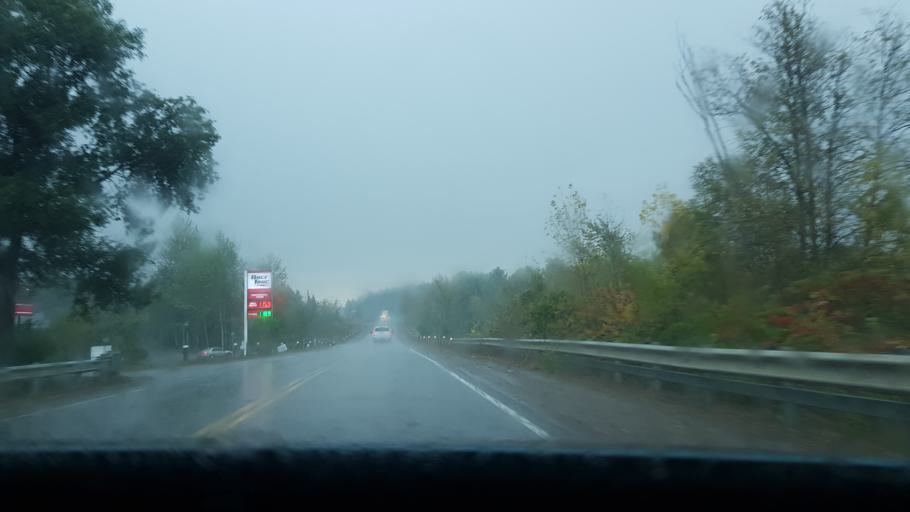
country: CA
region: Ontario
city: Omemee
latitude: 44.3421
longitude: -78.5413
